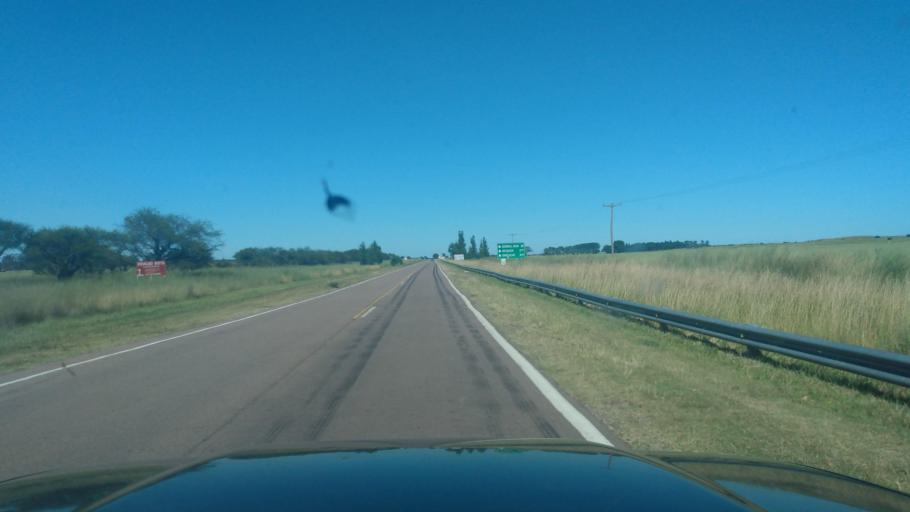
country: AR
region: La Pampa
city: General Acha
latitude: -37.3135
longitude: -64.2953
